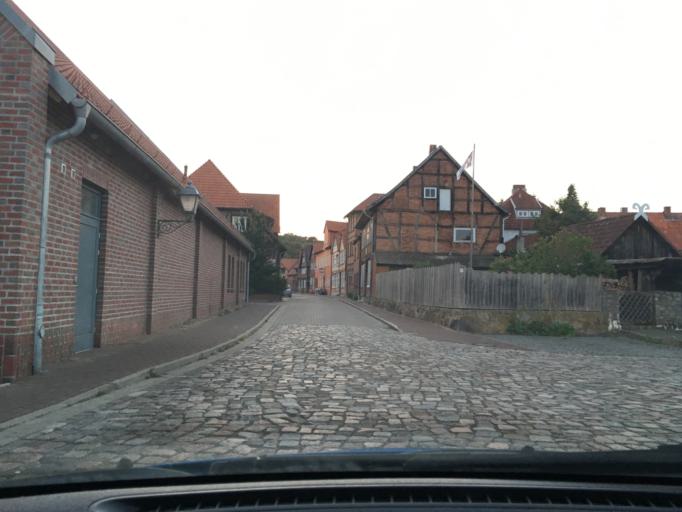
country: DE
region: Lower Saxony
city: Hitzacker
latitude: 53.1510
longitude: 11.0491
